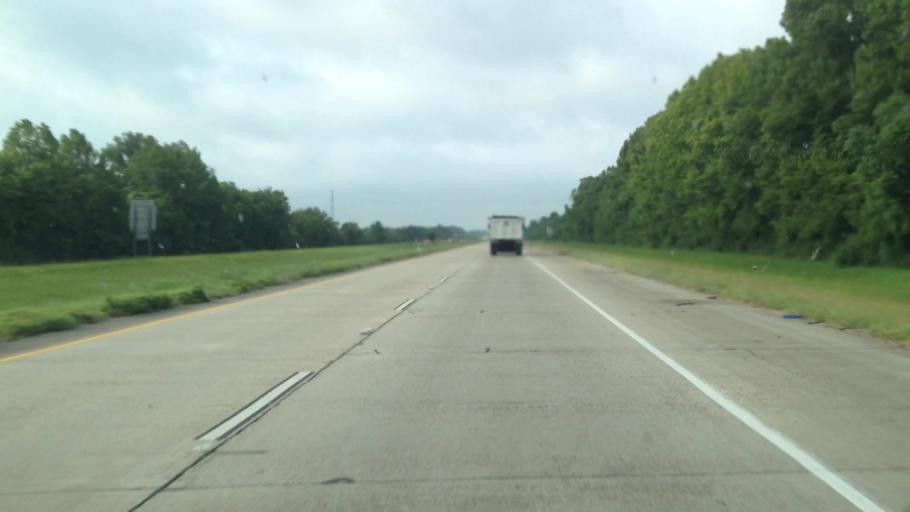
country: US
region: Louisiana
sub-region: Saint Landry Parish
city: Opelousas
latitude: 30.6322
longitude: -92.0481
